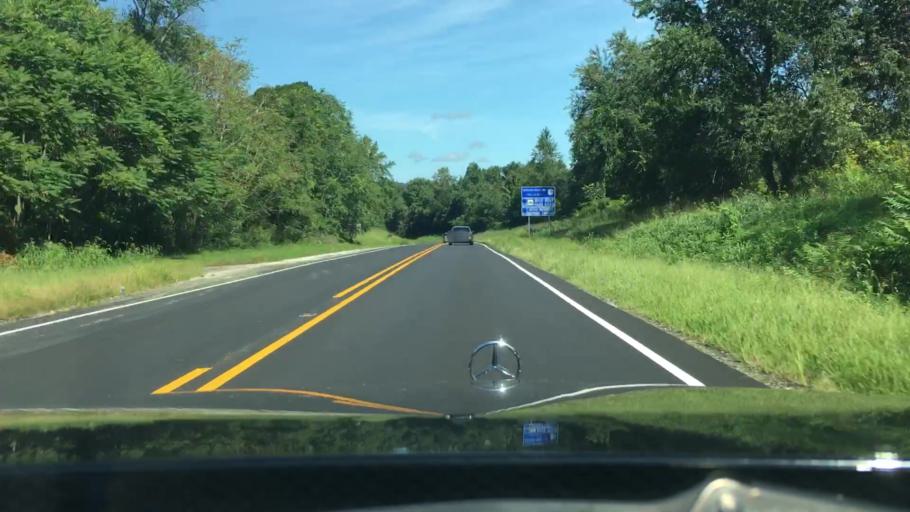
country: US
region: Virginia
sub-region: Nelson County
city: Nellysford
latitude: 37.9134
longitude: -78.8333
